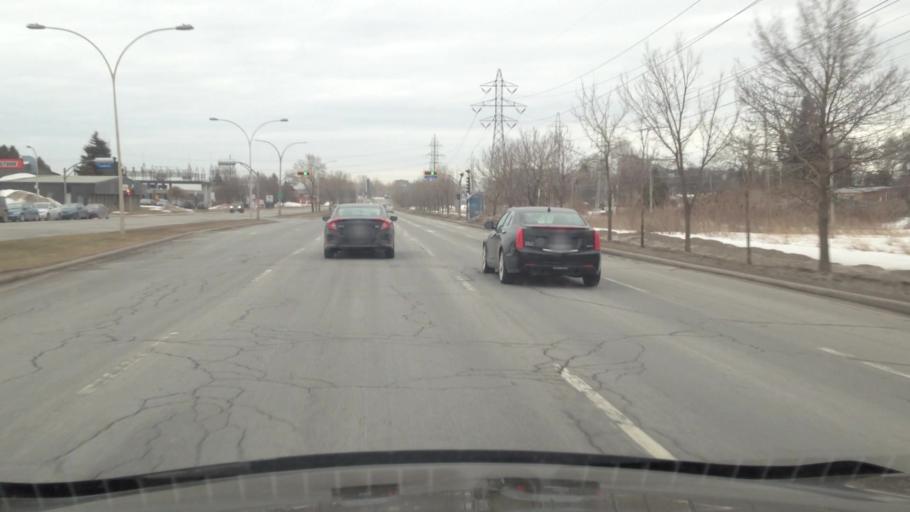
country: CA
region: Quebec
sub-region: Laval
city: Laval
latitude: 45.5779
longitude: -73.7281
